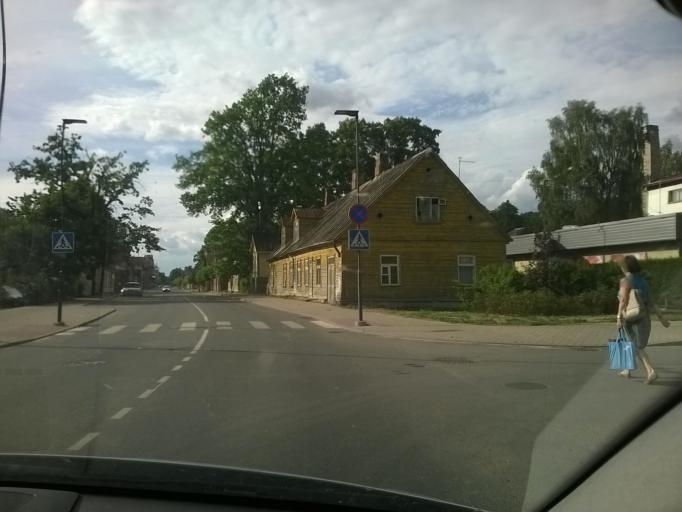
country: EE
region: Vorumaa
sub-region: Voru linn
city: Voru
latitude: 57.8415
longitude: 27.0017
